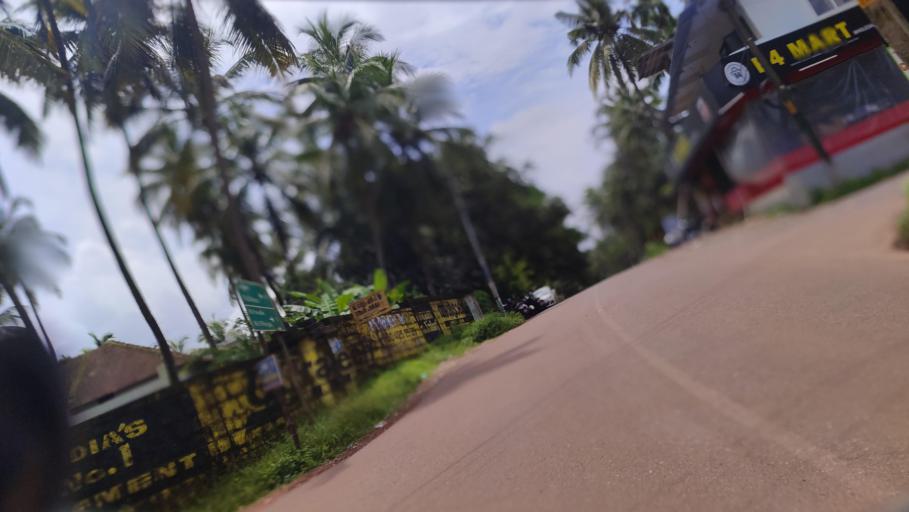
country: IN
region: Kerala
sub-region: Kasaragod District
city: Kannangad
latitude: 12.3931
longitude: 75.0489
